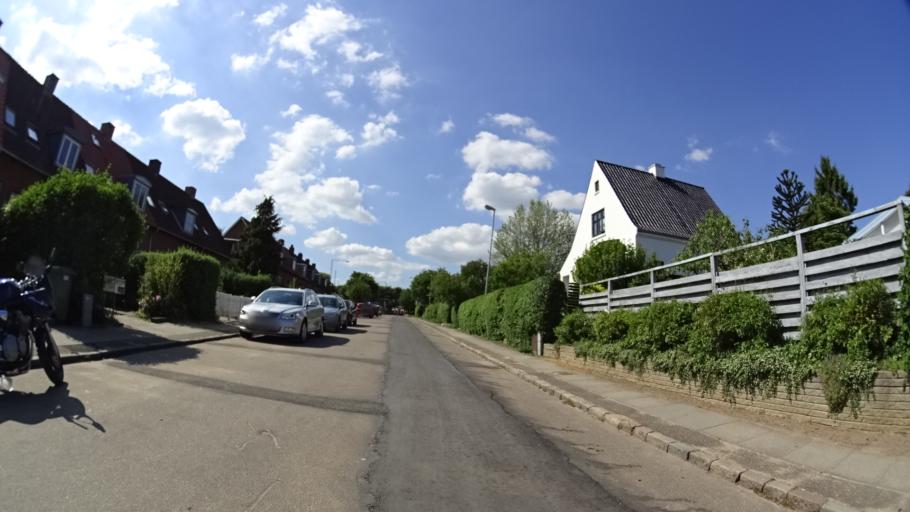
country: DK
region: Central Jutland
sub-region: Arhus Kommune
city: Stavtrup
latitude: 56.1529
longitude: 10.1458
